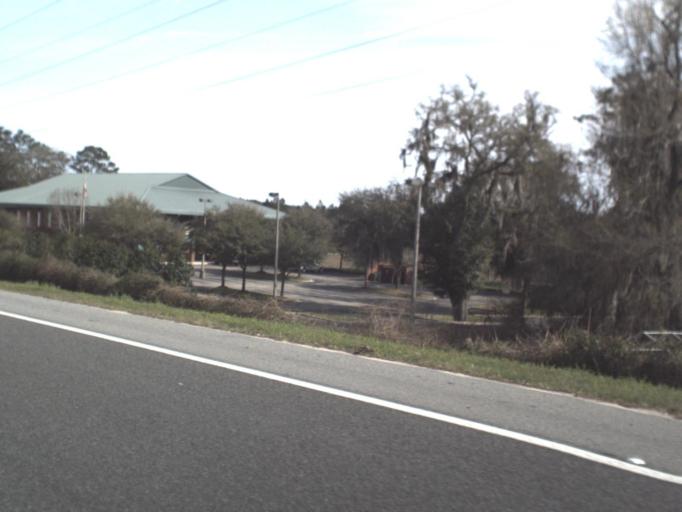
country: US
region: Florida
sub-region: Leon County
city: Tallahassee
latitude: 30.4781
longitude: -84.3532
